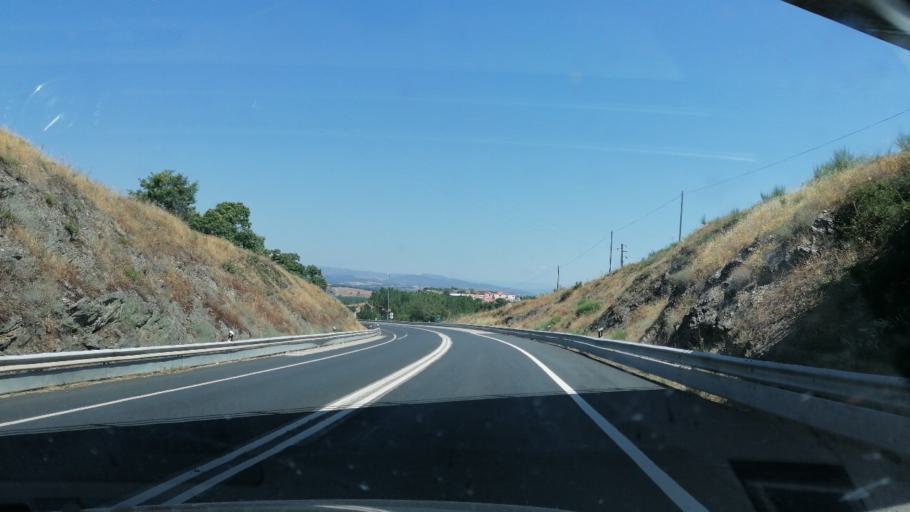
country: PT
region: Braganca
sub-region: Braganca Municipality
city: Braganca
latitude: 41.7646
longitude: -6.7923
